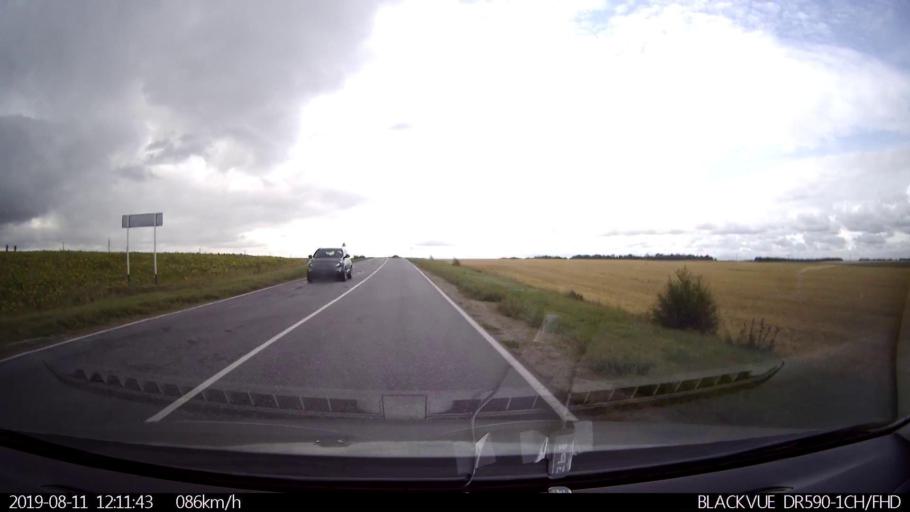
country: RU
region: Ulyanovsk
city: Silikatnyy
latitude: 53.9822
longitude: 48.0012
